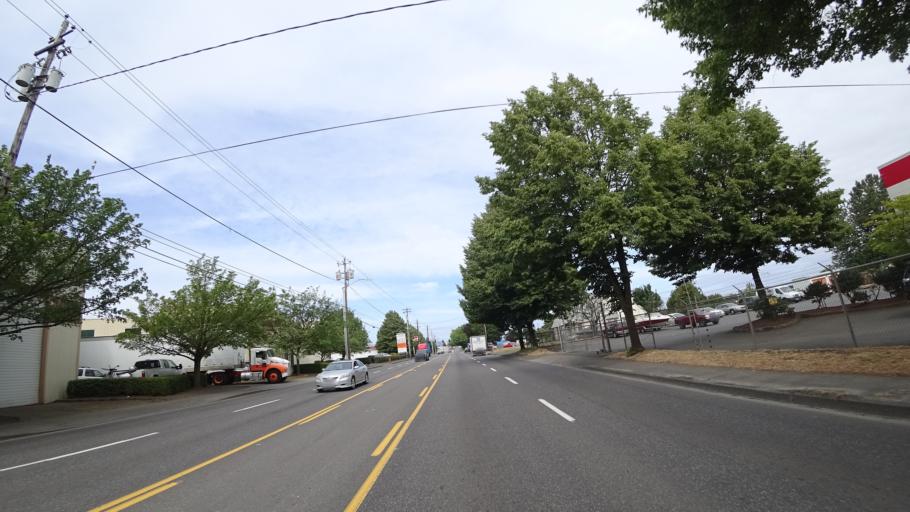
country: US
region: Oregon
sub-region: Multnomah County
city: Portland
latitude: 45.5761
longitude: -122.6417
